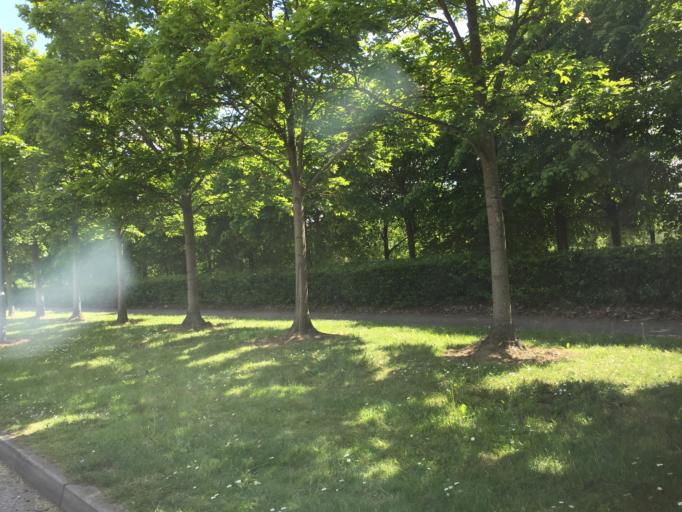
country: GB
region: England
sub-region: Milton Keynes
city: Wavendon
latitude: 52.0369
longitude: -0.6777
